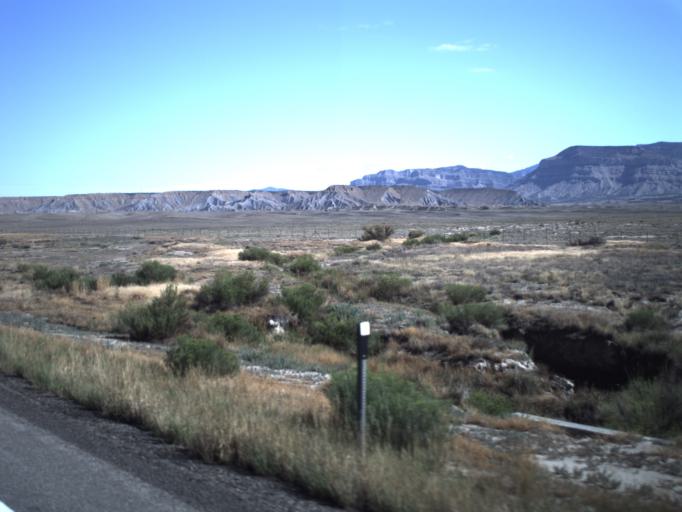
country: US
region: Utah
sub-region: Carbon County
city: East Carbon City
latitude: 39.3615
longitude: -110.3894
